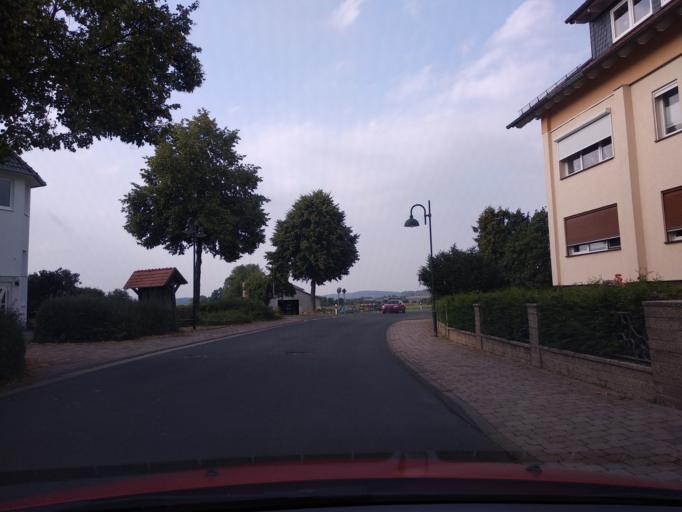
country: DE
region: Hesse
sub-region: Regierungsbezirk Kassel
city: Calden
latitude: 51.3853
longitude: 9.3643
